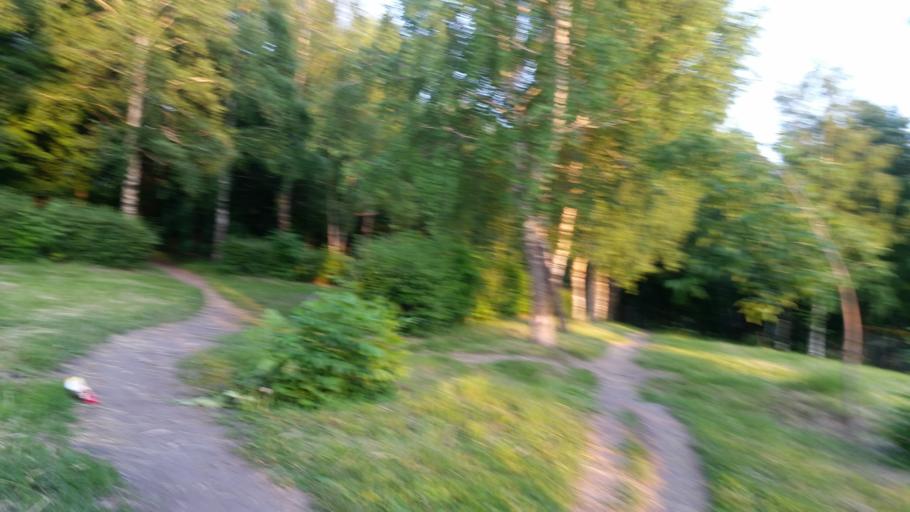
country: RU
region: Ulyanovsk
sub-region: Ulyanovskiy Rayon
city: Ulyanovsk
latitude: 54.3499
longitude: 48.3929
